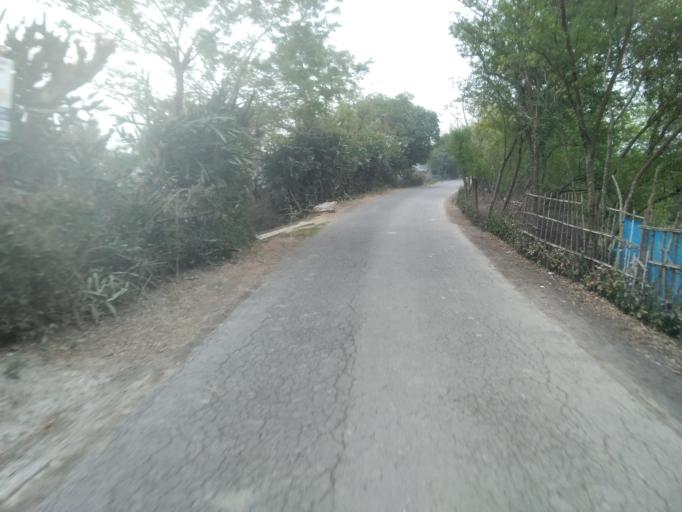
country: BD
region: Khulna
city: Satkhira
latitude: 22.5743
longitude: 89.0763
